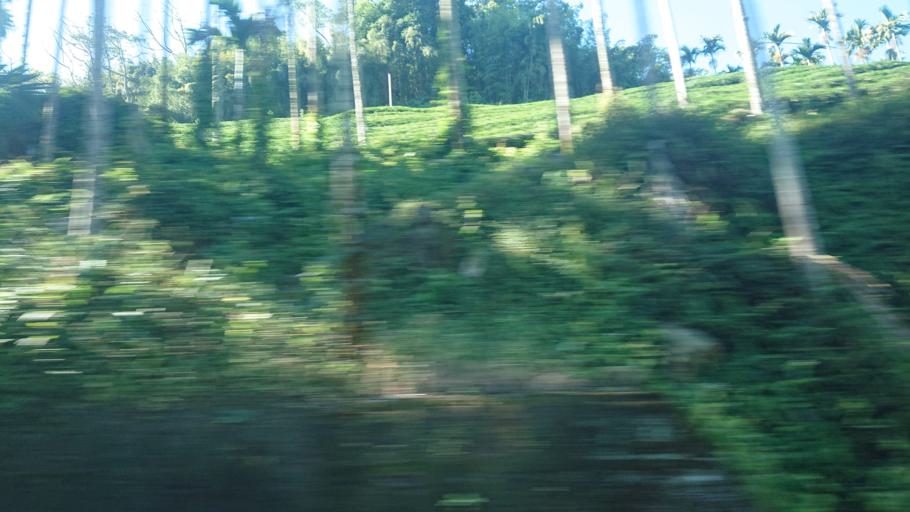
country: TW
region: Taiwan
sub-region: Chiayi
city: Jiayi Shi
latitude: 23.5348
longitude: 120.6411
